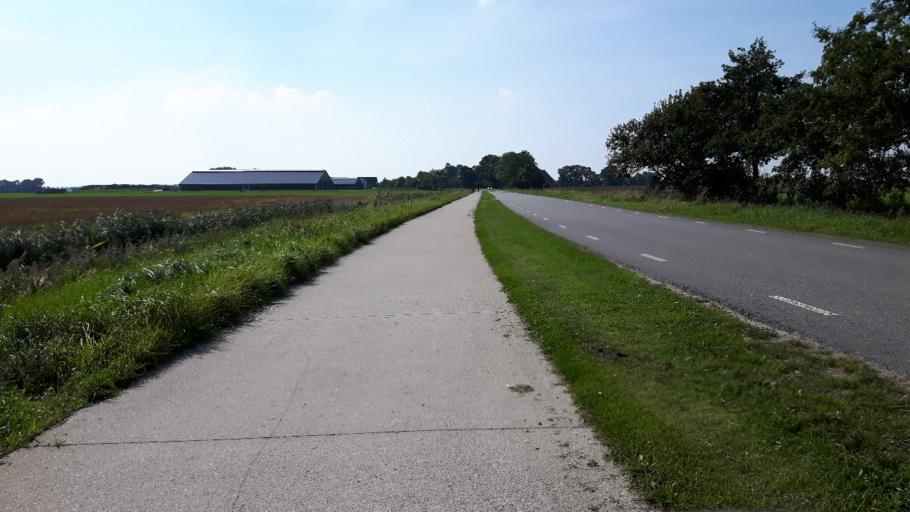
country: NL
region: Friesland
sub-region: Gemeente Franekeradeel
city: Tzummarum
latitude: 53.2172
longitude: 5.5750
